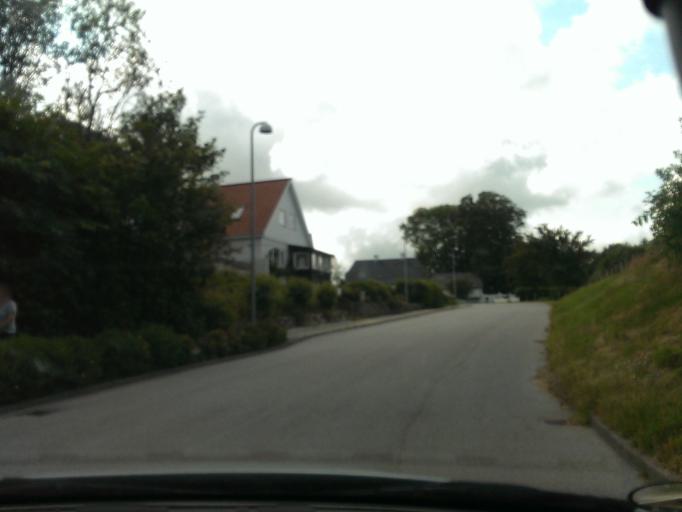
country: DK
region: North Denmark
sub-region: Hjorring Kommune
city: Vra
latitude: 57.3523
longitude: 9.9400
